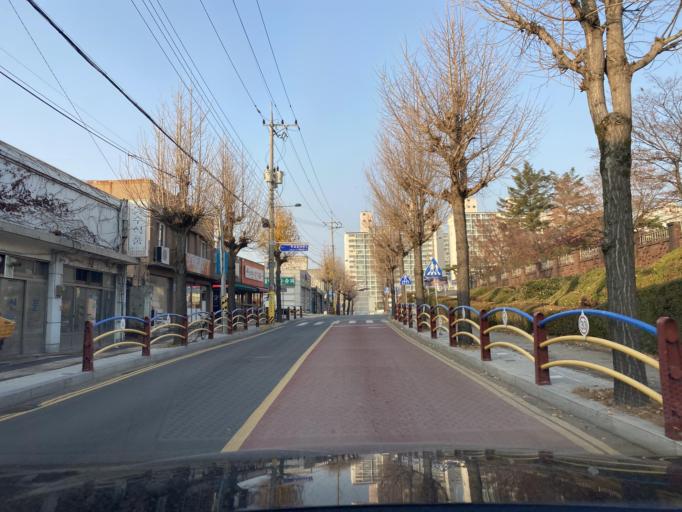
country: KR
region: Chungcheongnam-do
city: Yesan
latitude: 36.6841
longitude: 126.8327
